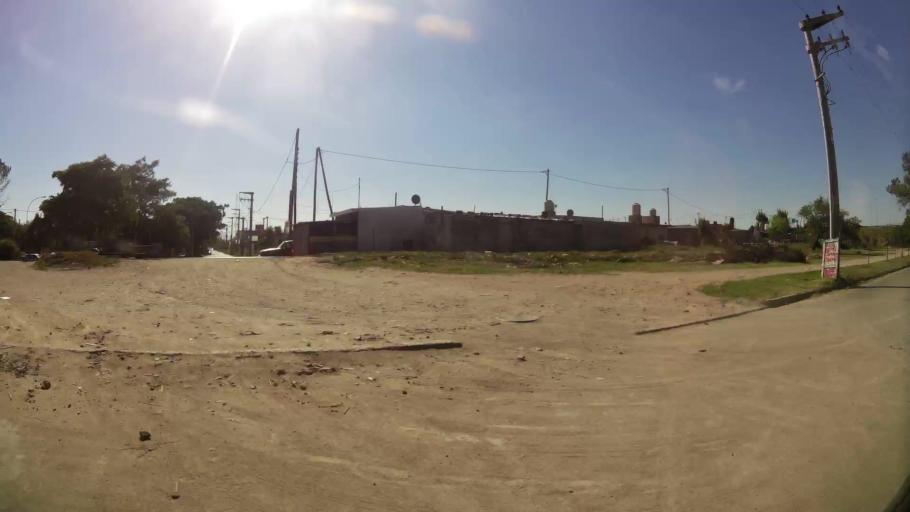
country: AR
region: Cordoba
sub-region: Departamento de Capital
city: Cordoba
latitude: -31.3573
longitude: -64.1858
